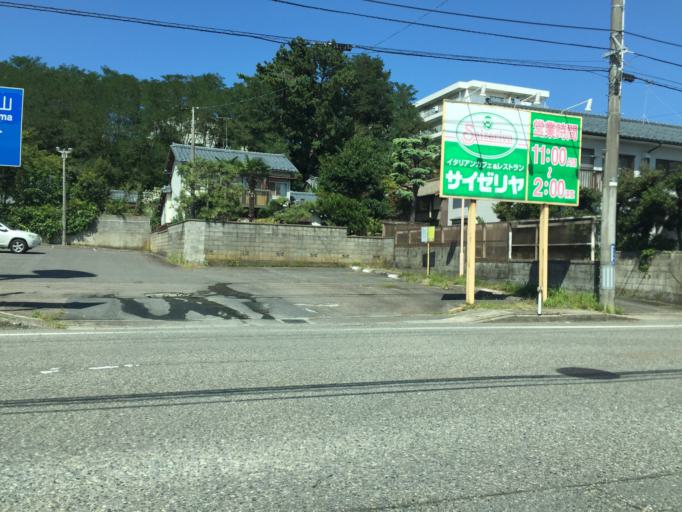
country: JP
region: Niigata
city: Niigata-shi
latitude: 37.8975
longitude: 139.0054
